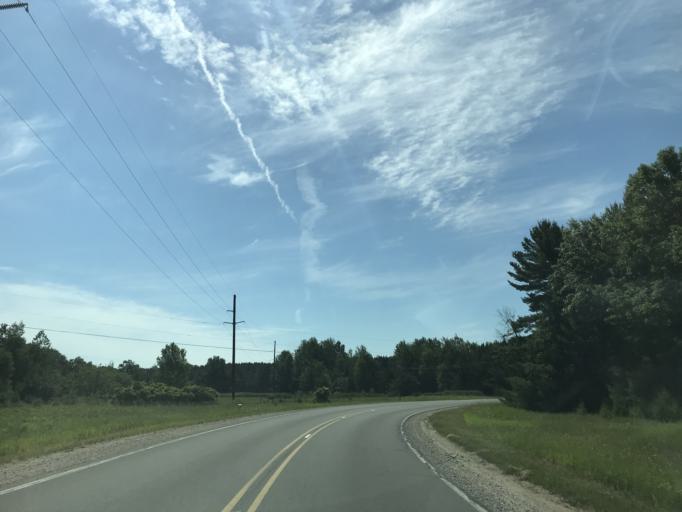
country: US
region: Michigan
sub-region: Grand Traverse County
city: Traverse City
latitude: 44.6580
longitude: -85.7179
